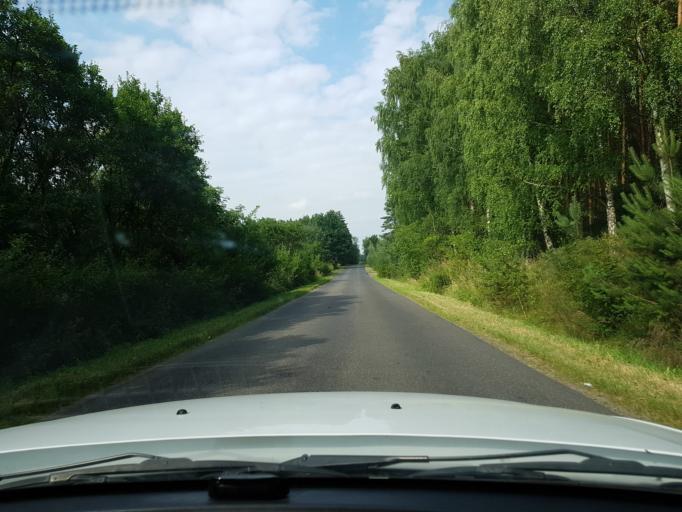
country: PL
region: West Pomeranian Voivodeship
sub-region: Powiat gryfinski
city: Chojna
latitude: 52.9702
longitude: 14.4619
